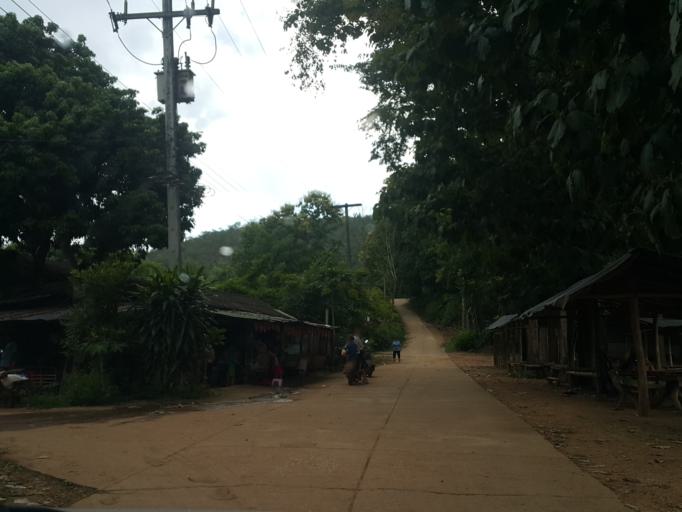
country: TH
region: Chiang Mai
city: Phrao
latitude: 19.3329
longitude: 99.1481
